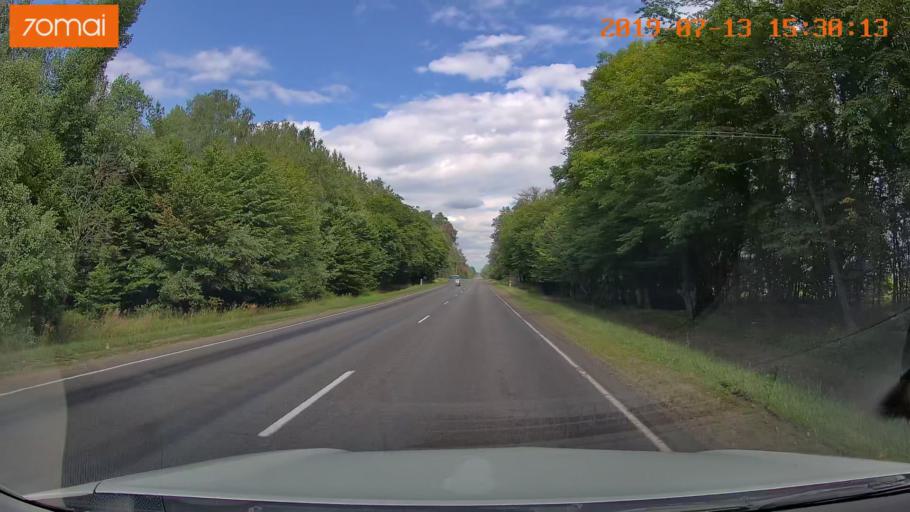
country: BY
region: Mogilev
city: Babruysk
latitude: 53.1099
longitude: 29.0830
